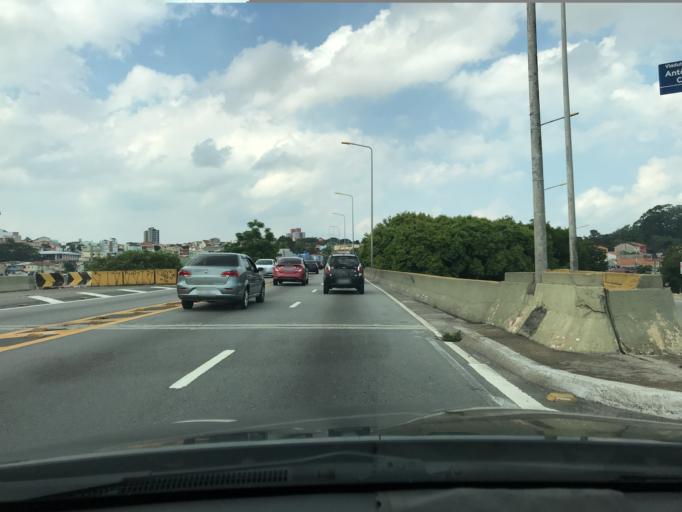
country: BR
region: Sao Paulo
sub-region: Santo Andre
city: Santo Andre
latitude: -23.6504
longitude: -46.5250
